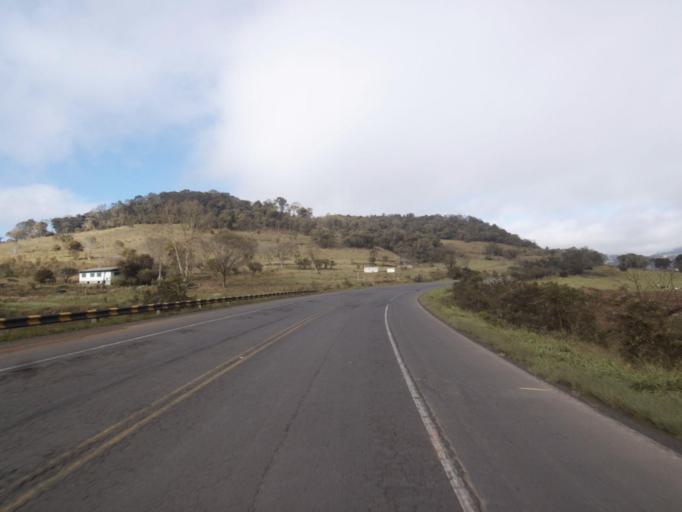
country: BR
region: Rio Grande do Sul
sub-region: Frederico Westphalen
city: Frederico Westphalen
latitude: -27.0218
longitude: -53.2293
